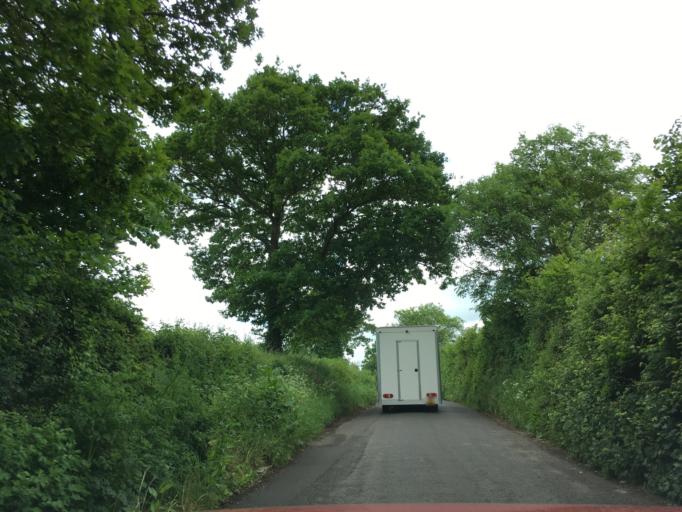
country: GB
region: England
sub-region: Somerset
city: Bishops Lydeard
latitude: 50.9690
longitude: -3.2006
